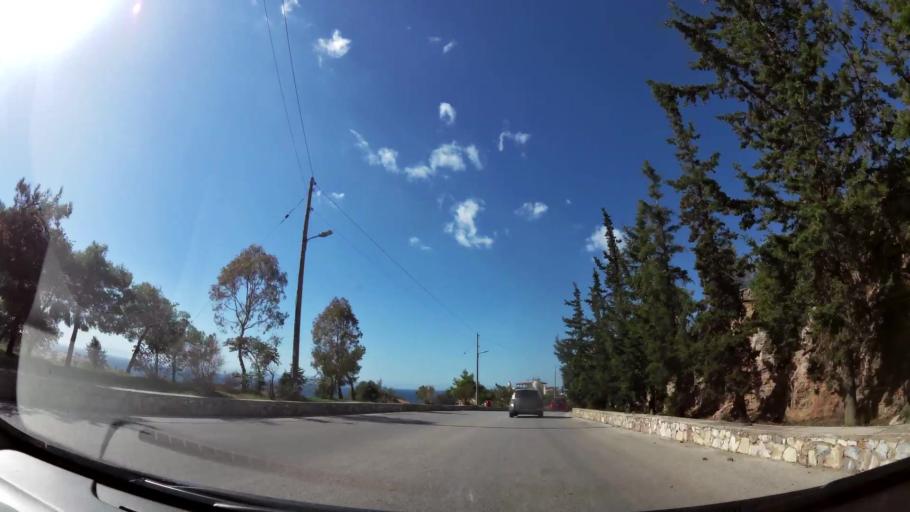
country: GR
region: Attica
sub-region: Nomarchia Anatolikis Attikis
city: Voula
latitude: 37.8528
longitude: 23.7763
